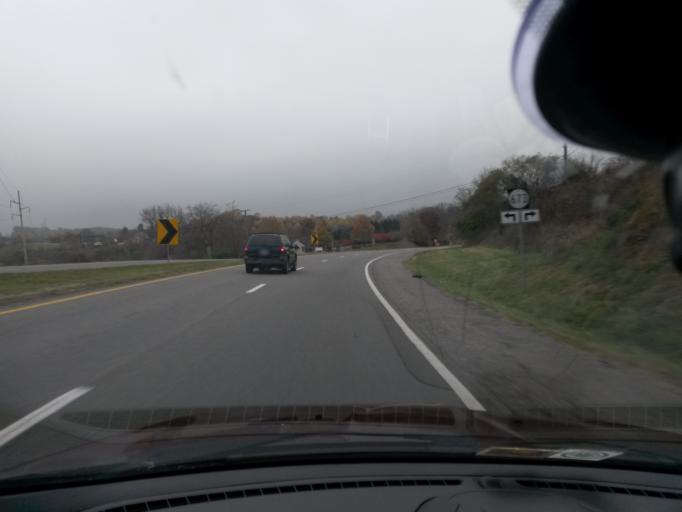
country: US
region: Virginia
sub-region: Botetourt County
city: Daleville
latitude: 37.4299
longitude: -79.9040
